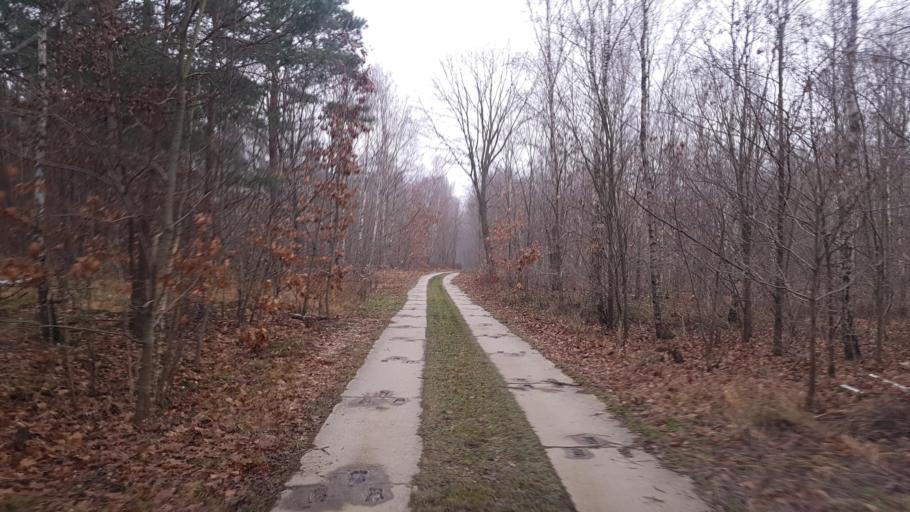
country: DE
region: Brandenburg
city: Plessa
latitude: 51.4961
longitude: 13.6382
